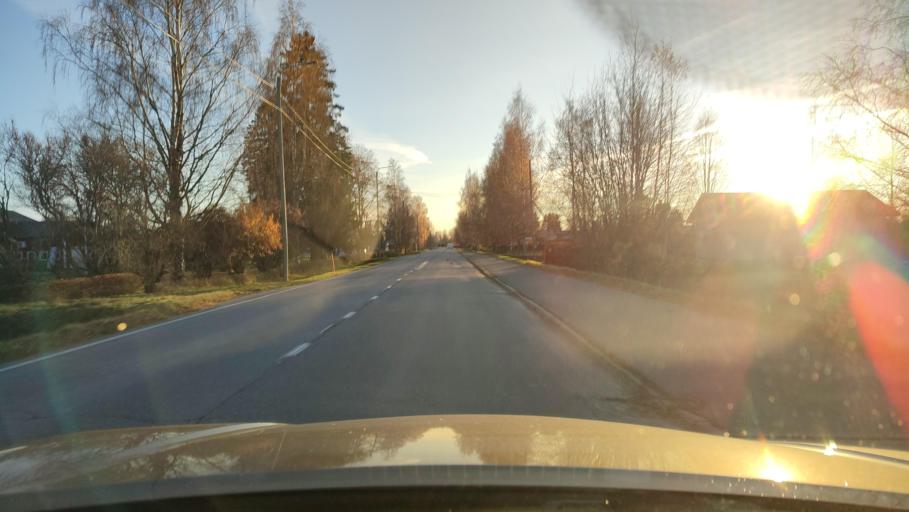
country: FI
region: Ostrobothnia
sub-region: Sydosterbotten
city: Naerpes
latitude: 62.6066
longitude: 21.4614
